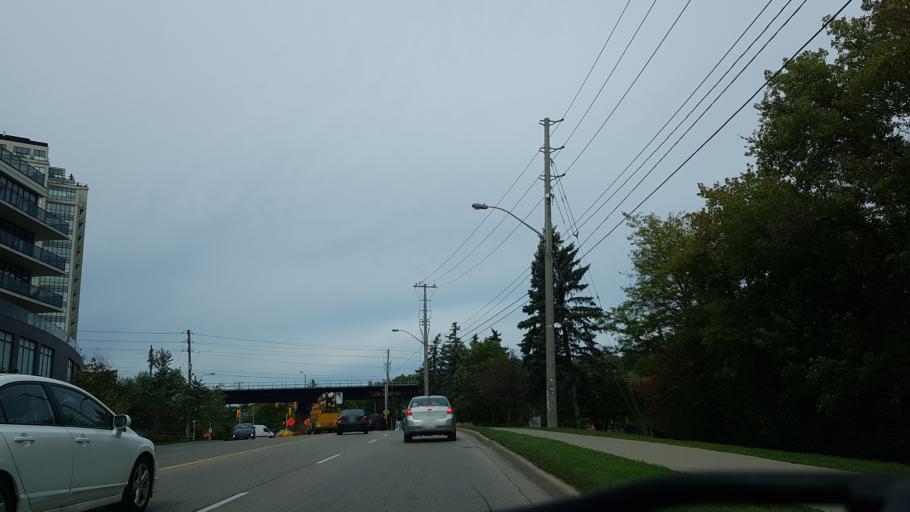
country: CA
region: Ontario
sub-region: Wellington County
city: Guelph
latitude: 43.5459
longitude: -80.2432
